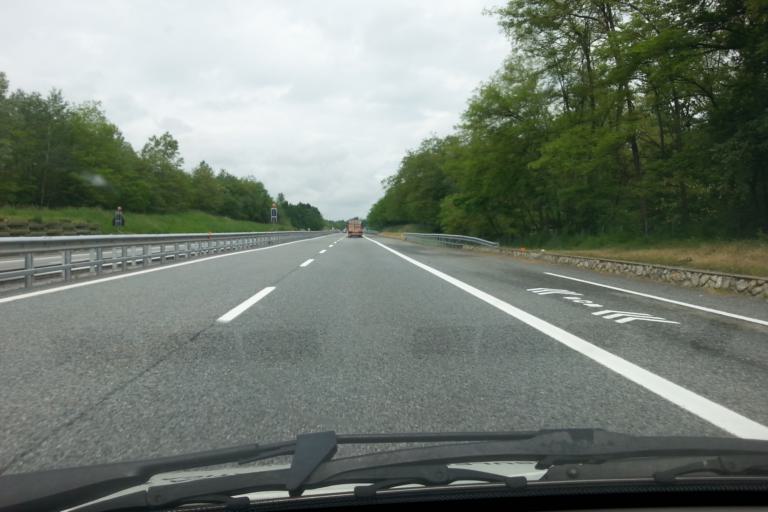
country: IT
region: Piedmont
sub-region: Provincia di Cuneo
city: Lesegno
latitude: 44.3946
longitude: 7.9872
